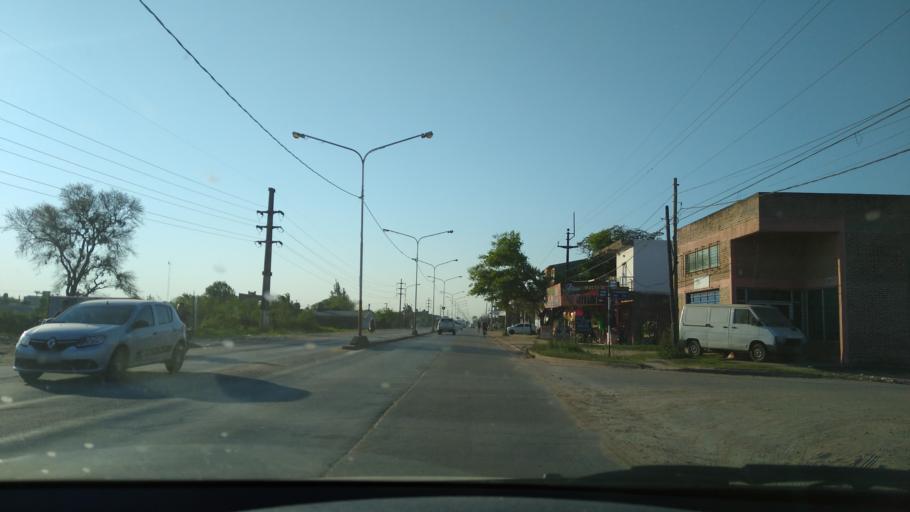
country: AR
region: Chaco
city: Barranqueras
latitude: -27.4927
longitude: -58.9538
